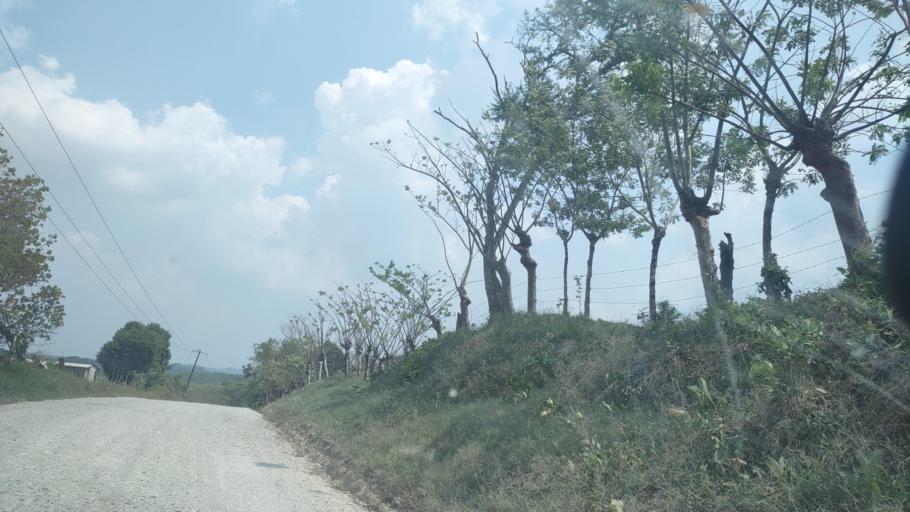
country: MX
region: Tabasco
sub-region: Huimanguillo
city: Francisco Rueda
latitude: 17.6100
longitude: -93.9121
